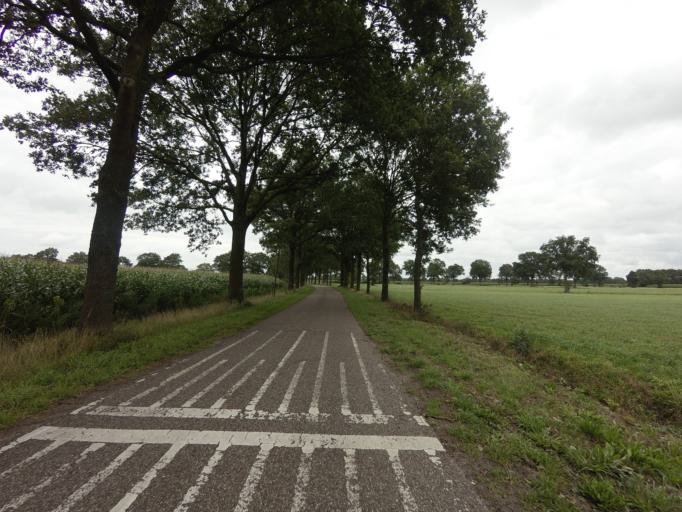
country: NL
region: Friesland
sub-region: Gemeente Weststellingwerf
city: Steggerda
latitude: 52.8653
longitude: 6.0742
